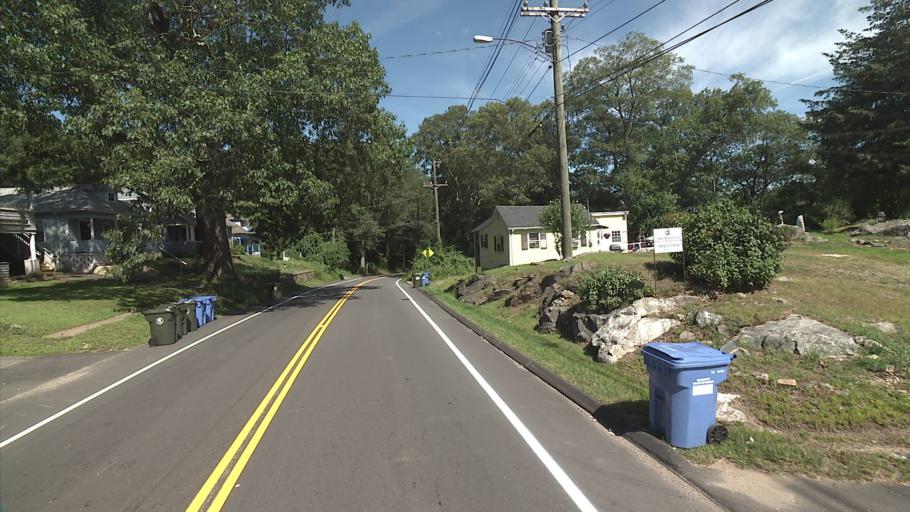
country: US
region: Connecticut
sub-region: New London County
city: Lisbon
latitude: 41.5796
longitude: -72.0453
